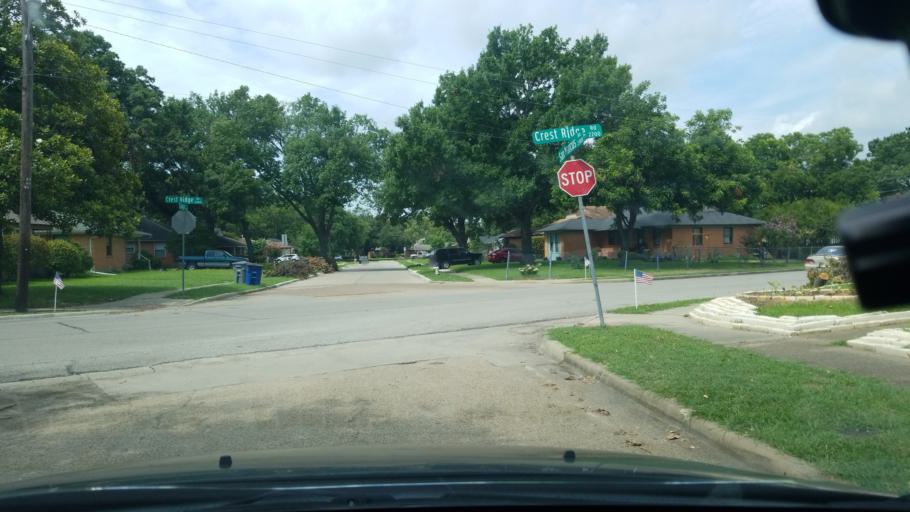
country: US
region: Texas
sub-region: Dallas County
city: Garland
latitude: 32.8311
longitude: -96.6775
